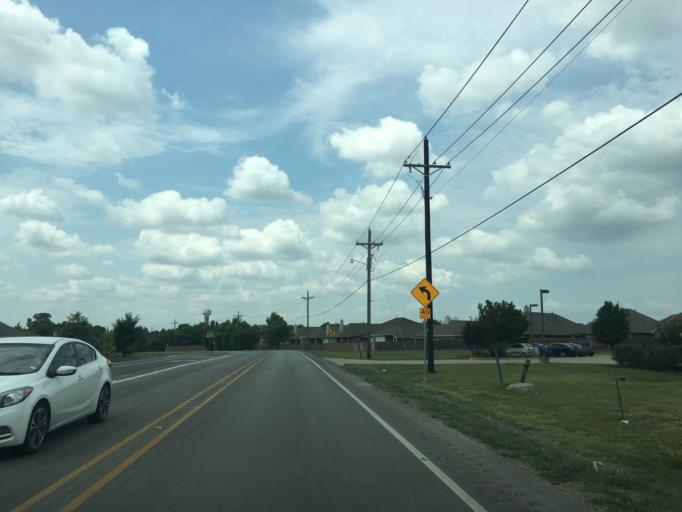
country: US
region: Texas
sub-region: Rockwall County
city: Fate
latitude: 32.9508
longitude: -96.3806
